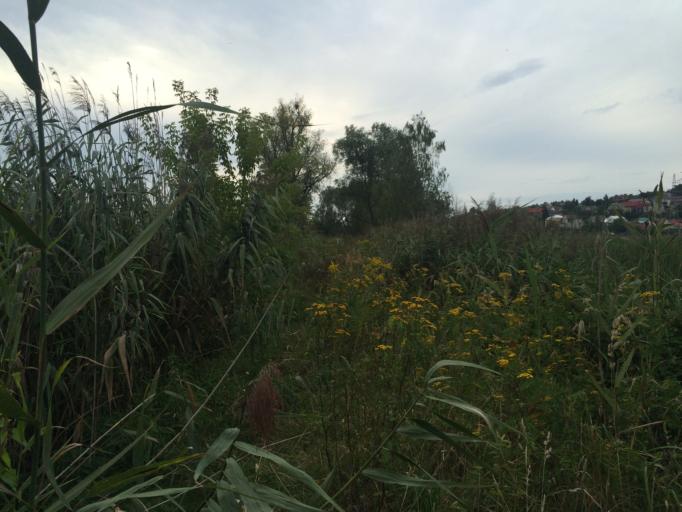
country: PL
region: Swietokrzyskie
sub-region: Powiat starachowicki
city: Starachowice
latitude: 51.0494
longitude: 21.0572
